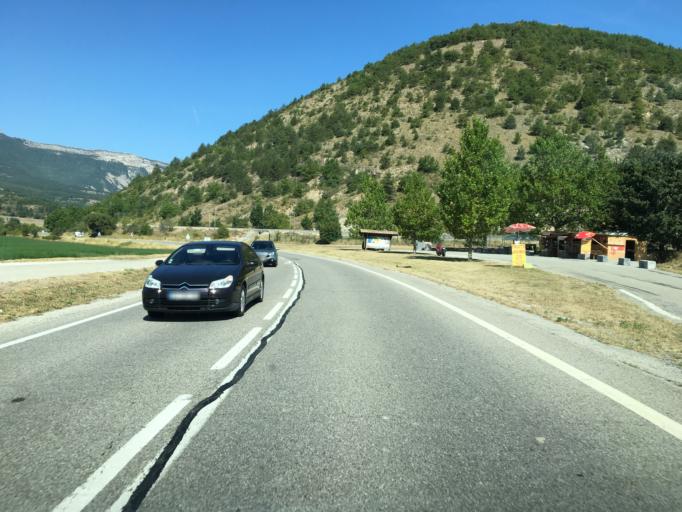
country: FR
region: Provence-Alpes-Cote d'Azur
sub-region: Departement des Hautes-Alpes
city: Serres
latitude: 44.3772
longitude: 5.7487
